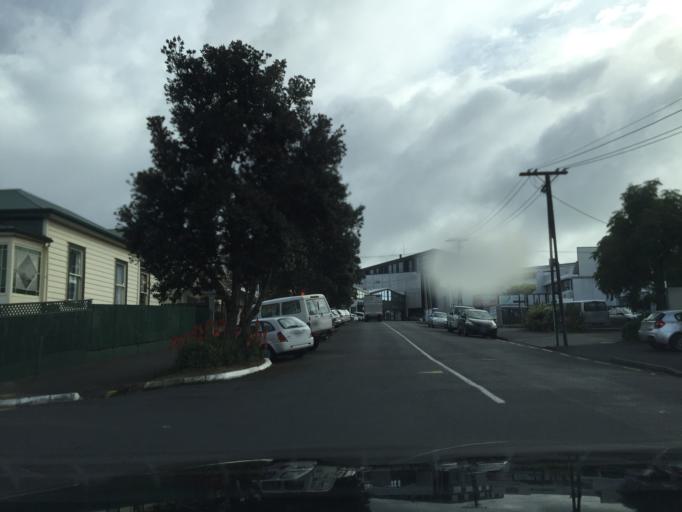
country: NZ
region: Auckland
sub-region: Auckland
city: Auckland
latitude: -36.8584
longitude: 174.7469
